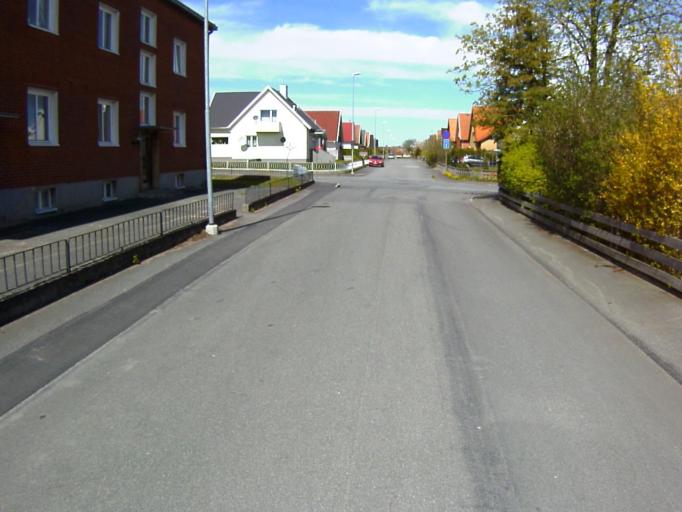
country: SE
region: Skane
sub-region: Kristianstads Kommun
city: Kristianstad
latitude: 56.0517
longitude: 14.1533
